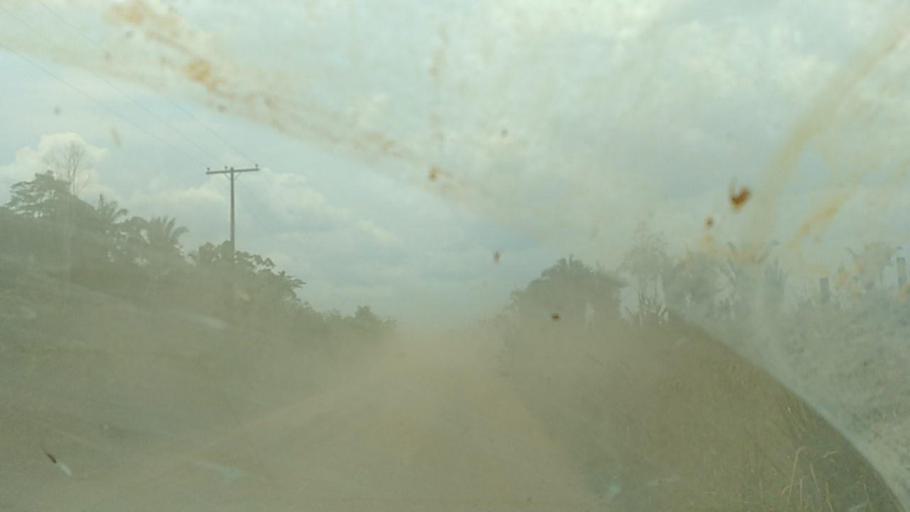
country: BR
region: Rondonia
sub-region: Porto Velho
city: Porto Velho
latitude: -8.9437
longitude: -64.3076
